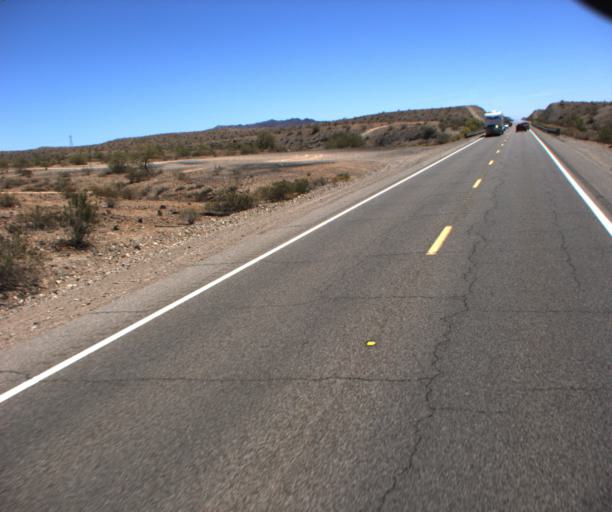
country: US
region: Arizona
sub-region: Mohave County
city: Lake Havasu City
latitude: 34.4339
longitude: -114.2191
